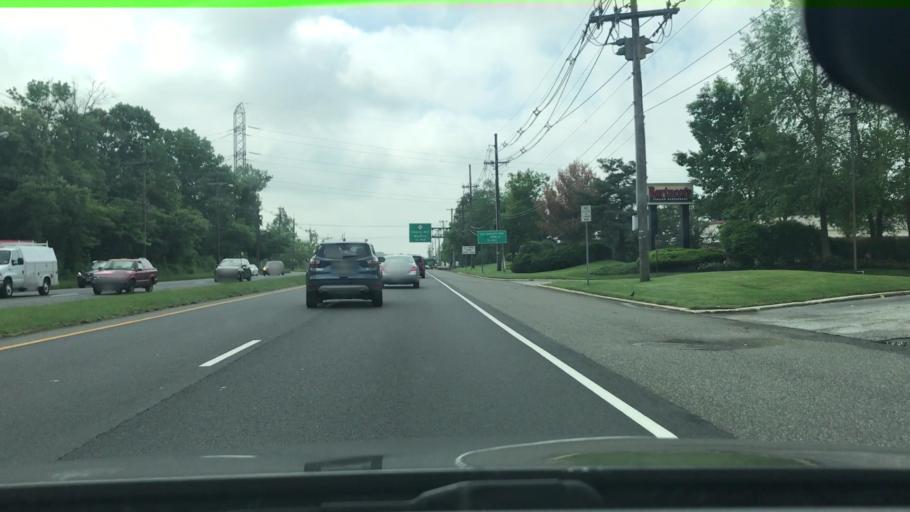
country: US
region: New Jersey
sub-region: Burlington County
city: Marlton
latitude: 39.9019
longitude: -74.9344
